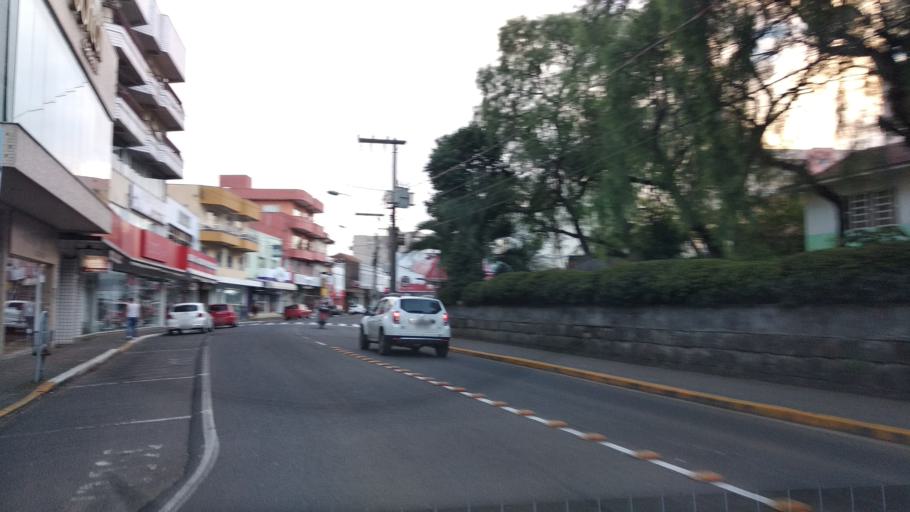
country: BR
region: Santa Catarina
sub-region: Videira
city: Videira
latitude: -27.0021
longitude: -51.1577
